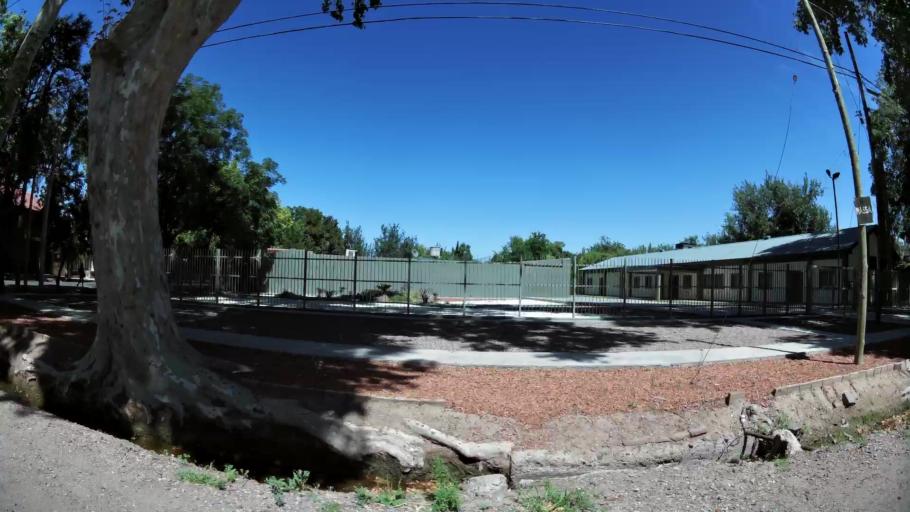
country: AR
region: Mendoza
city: Villa Nueva
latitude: -32.8674
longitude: -68.7858
